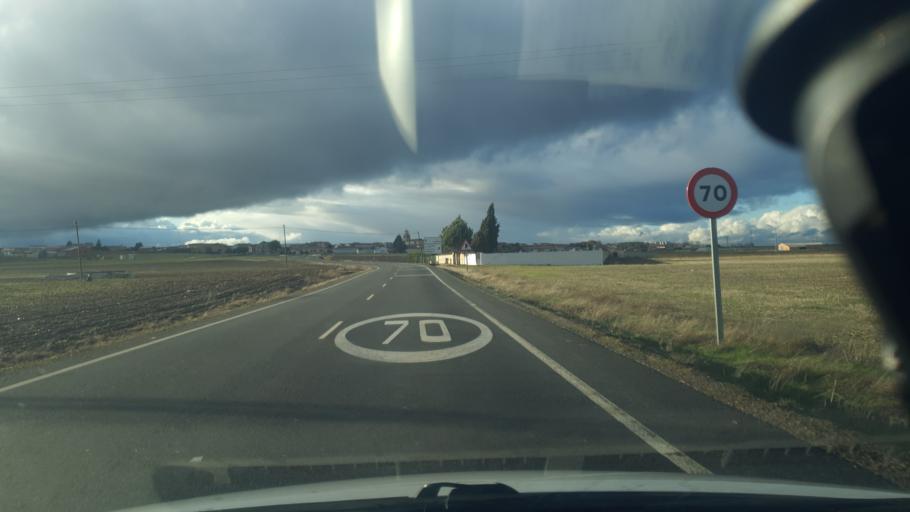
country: ES
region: Castille and Leon
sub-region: Provincia de Segovia
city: Santiuste de San Juan Bautista
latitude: 41.1539
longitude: -4.5624
